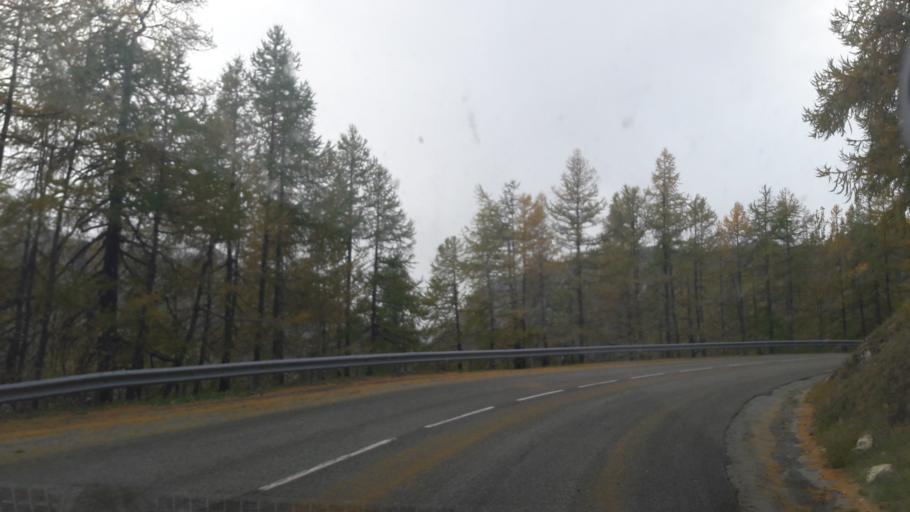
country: FR
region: Rhone-Alpes
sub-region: Departement de la Savoie
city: Tignes
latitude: 45.4866
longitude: 6.9285
